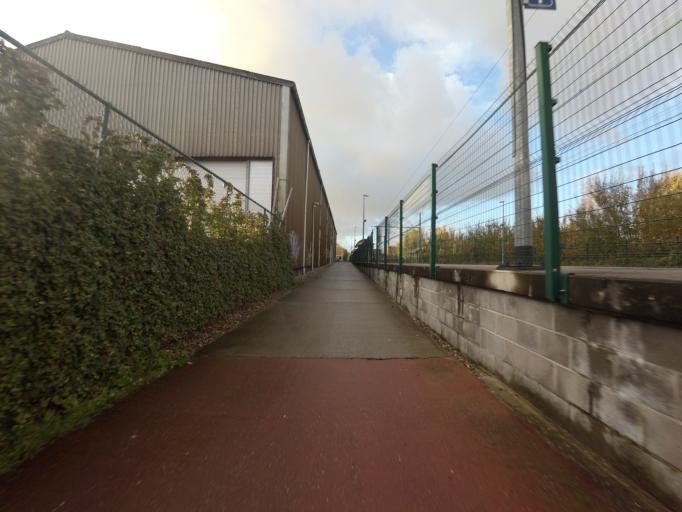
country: BE
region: Flanders
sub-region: Provincie Antwerpen
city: Niel
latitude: 51.1107
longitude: 4.3405
